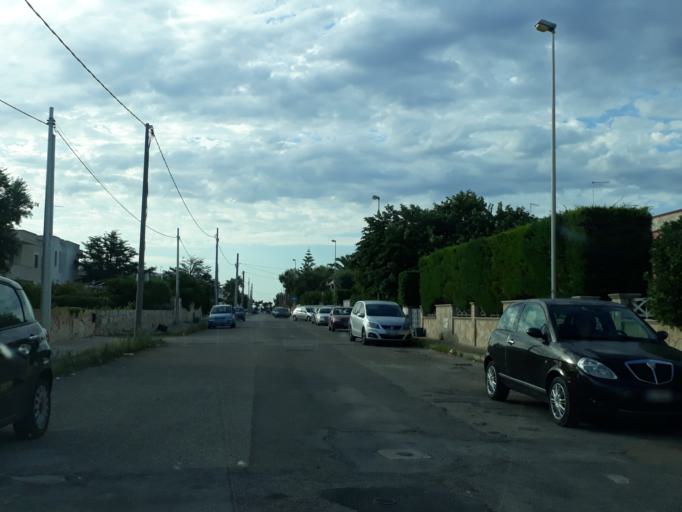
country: IT
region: Apulia
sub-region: Provincia di Brindisi
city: Carovigno
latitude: 40.7566
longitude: 17.6972
